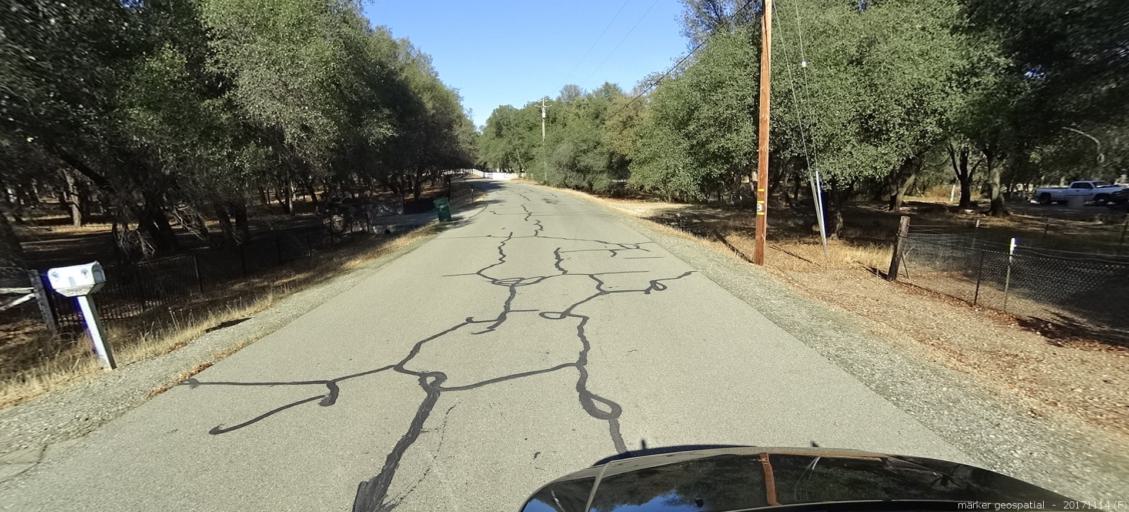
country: US
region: California
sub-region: Shasta County
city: Anderson
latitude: 40.3857
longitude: -122.4472
